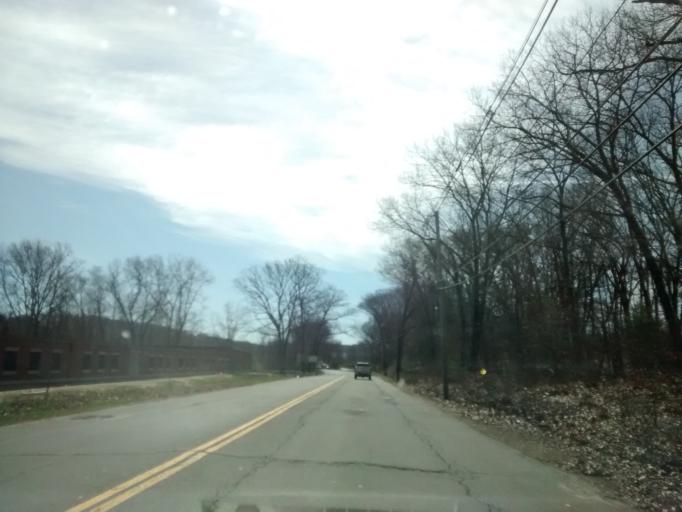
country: US
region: Massachusetts
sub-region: Worcester County
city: Millbury
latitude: 42.1827
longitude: -71.7372
